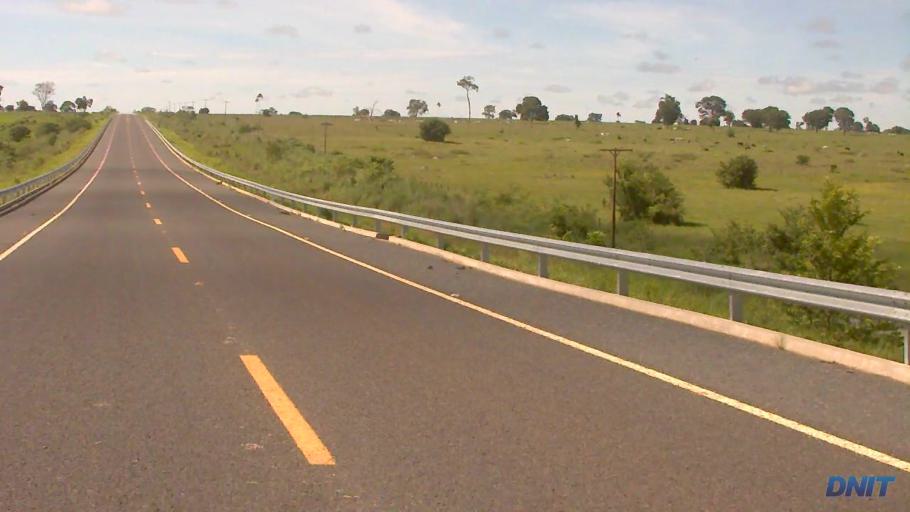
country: BR
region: Goias
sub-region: Sao Miguel Do Araguaia
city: Sao Miguel do Araguaia
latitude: -13.3437
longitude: -50.1514
